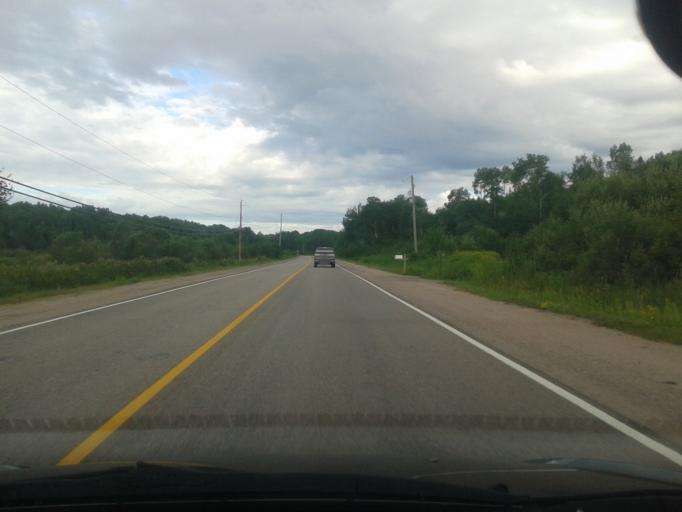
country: CA
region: Ontario
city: Powassan
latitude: 46.1899
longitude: -79.3089
